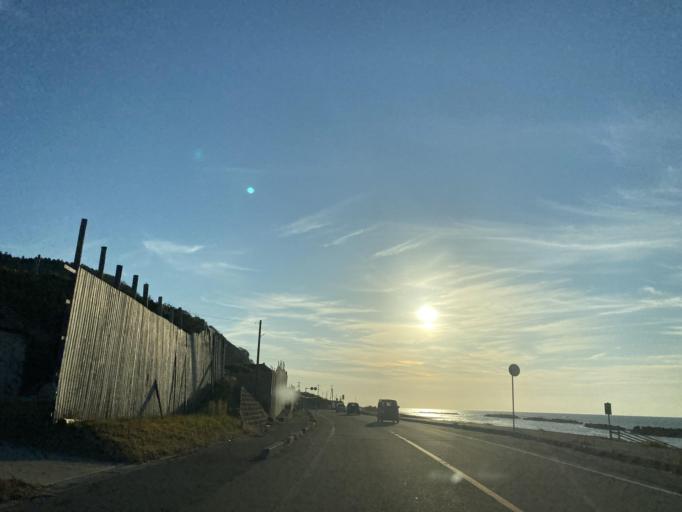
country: JP
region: Niigata
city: Kashiwazaki
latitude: 37.4982
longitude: 138.6408
